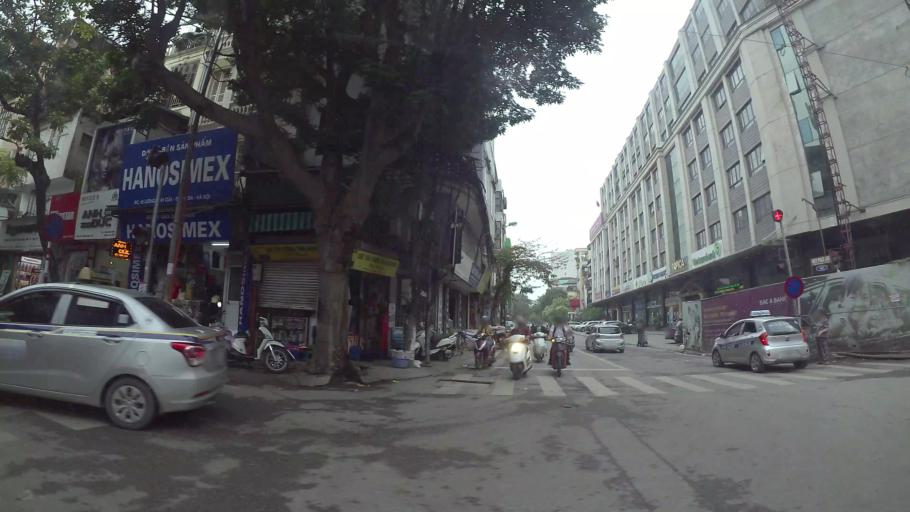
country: VN
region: Ha Noi
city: Hai BaTrung
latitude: 21.0035
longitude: 105.8359
